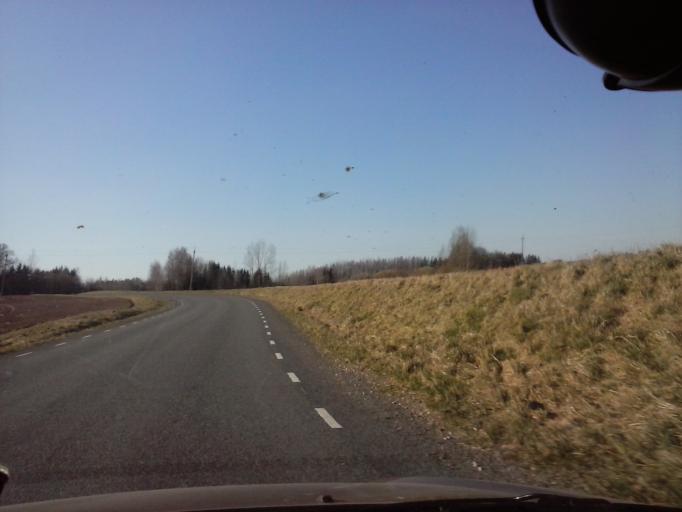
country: EE
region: Tartu
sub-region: UElenurme vald
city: Ulenurme
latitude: 58.1592
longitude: 26.8515
